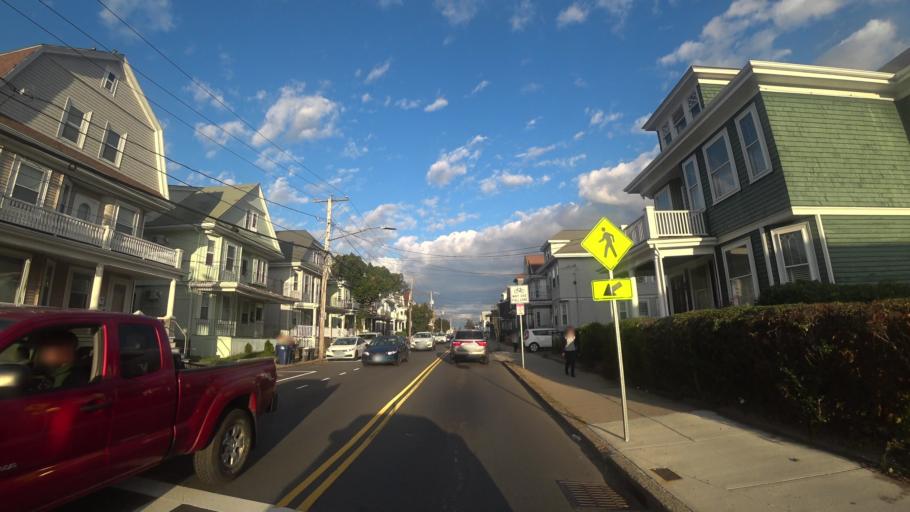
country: US
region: Massachusetts
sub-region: Suffolk County
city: Winthrop
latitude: 42.3845
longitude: -71.0005
